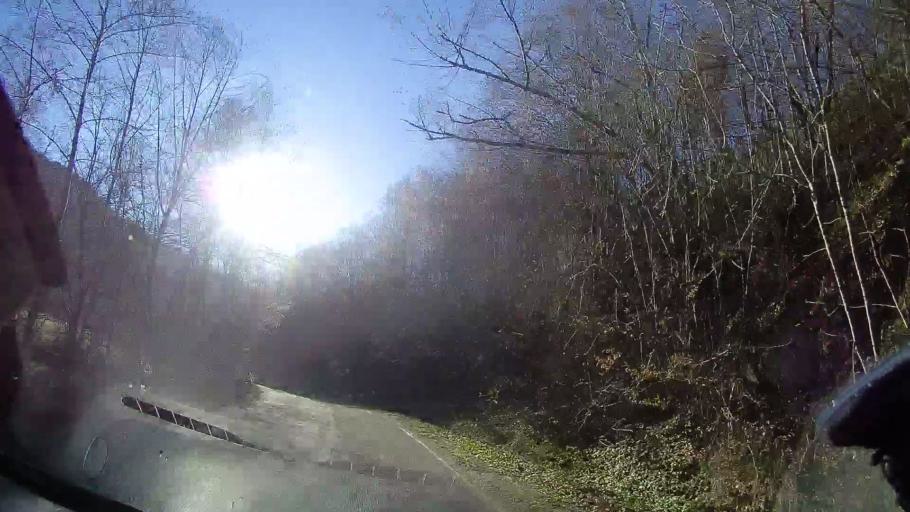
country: RO
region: Cluj
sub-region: Comuna Sacueu
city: Sacuieu
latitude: 46.8512
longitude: 22.8614
